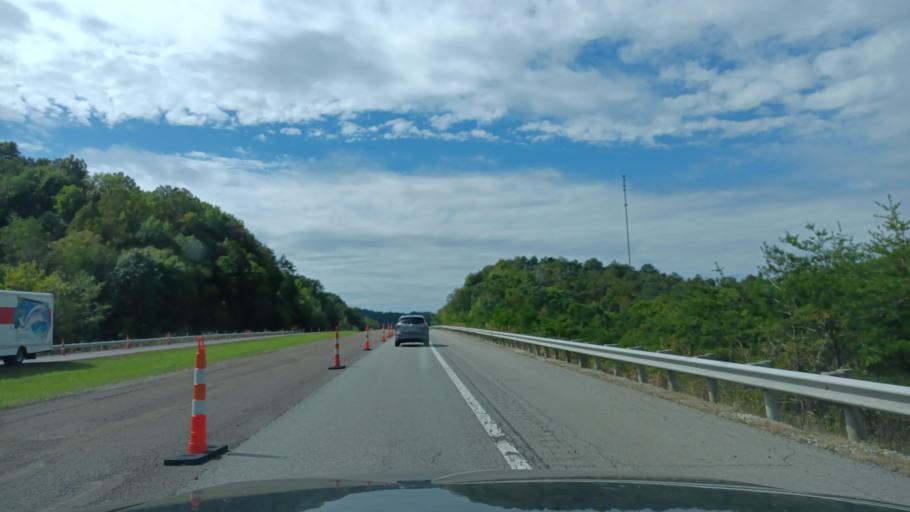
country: US
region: West Virginia
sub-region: Ritchie County
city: Harrisville
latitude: 39.2618
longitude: -81.1275
